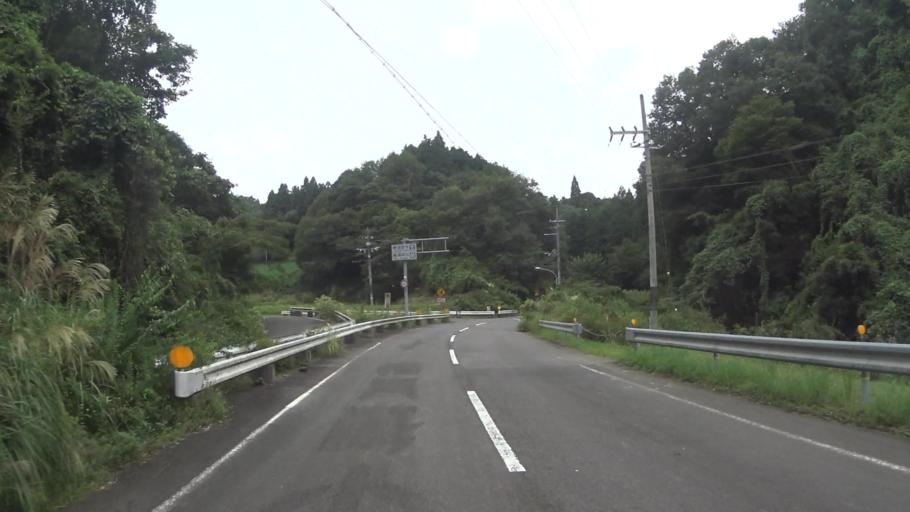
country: JP
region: Kyoto
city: Uji
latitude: 34.8549
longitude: 135.9390
